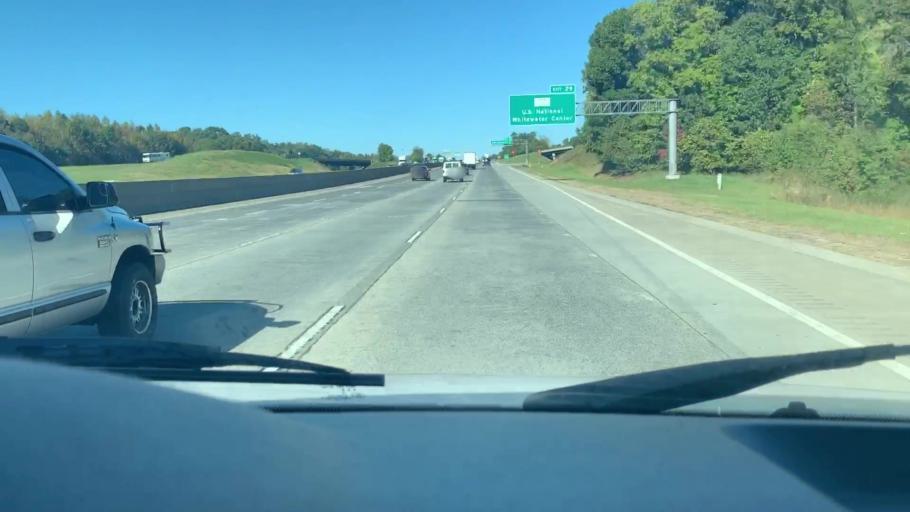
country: US
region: North Carolina
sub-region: Gaston County
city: Mount Holly
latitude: 35.2503
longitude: -80.9715
